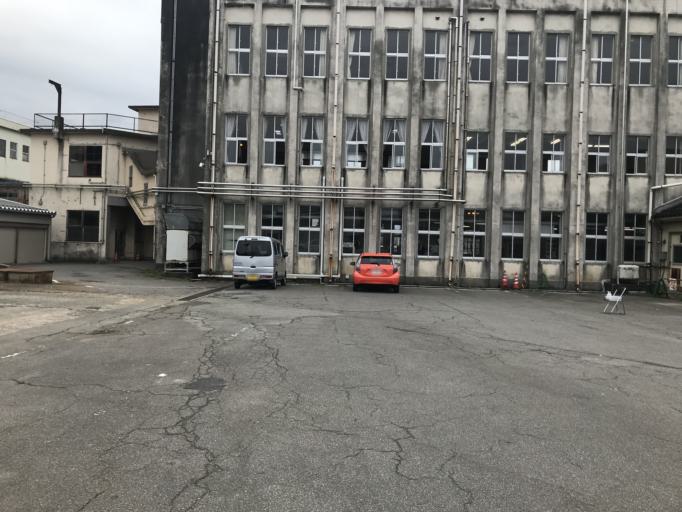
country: JP
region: Toyama
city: Nyuzen
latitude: 36.8739
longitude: 137.4494
